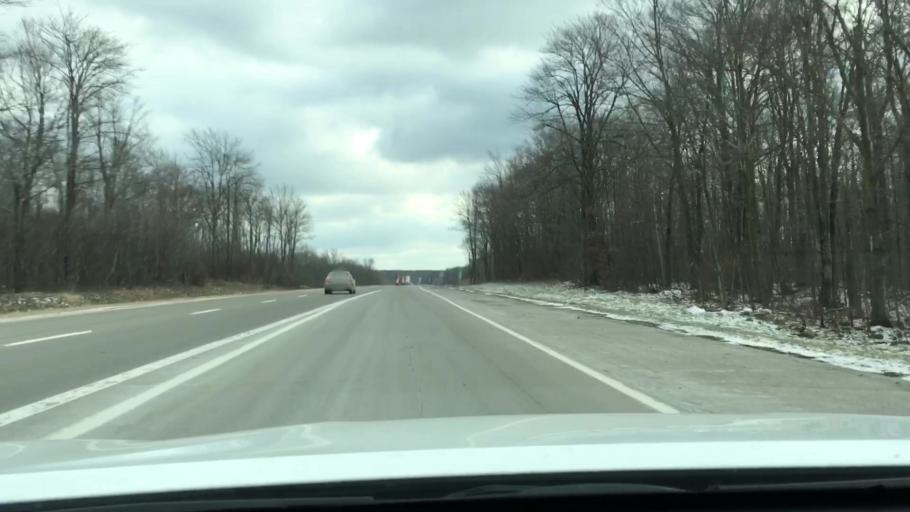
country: US
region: Pennsylvania
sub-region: Lackawanna County
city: Moscow
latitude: 41.2278
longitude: -75.4945
